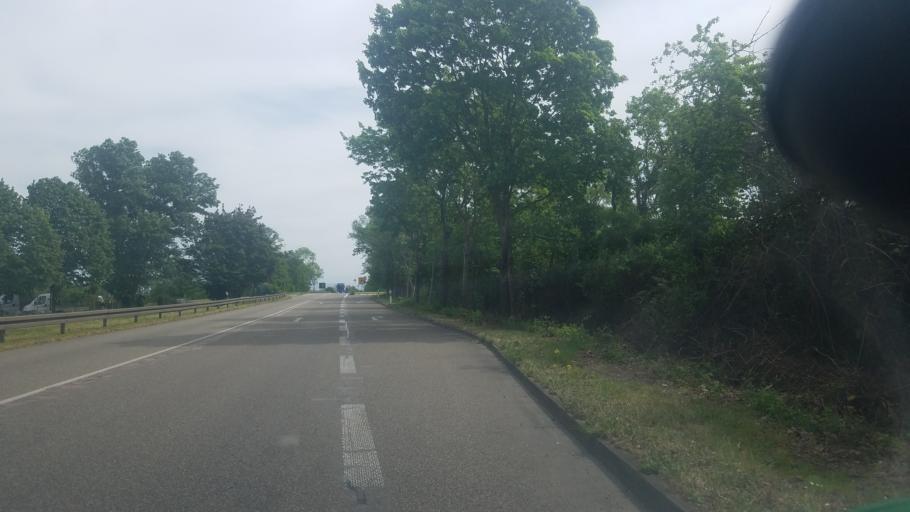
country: DE
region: Baden-Wuerttemberg
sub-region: Freiburg Region
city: Kehl
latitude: 48.5809
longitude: 7.8194
